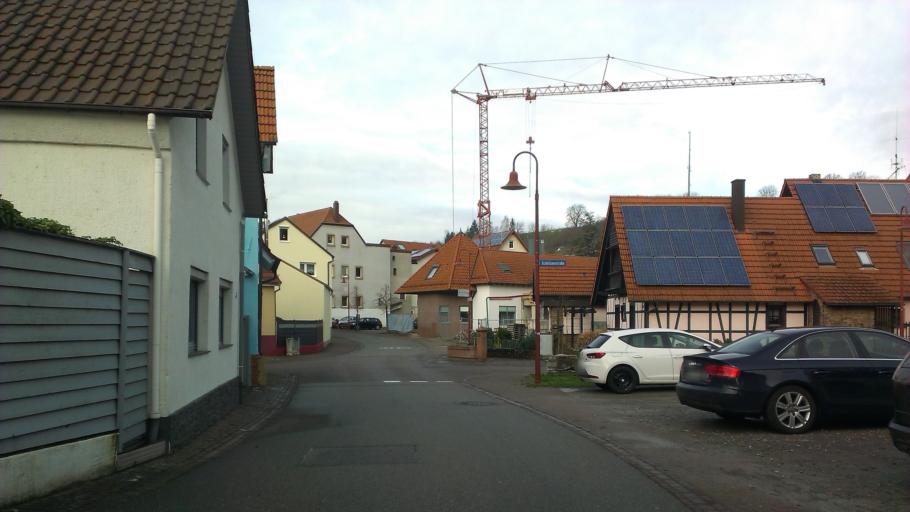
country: DE
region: Baden-Wuerttemberg
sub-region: Karlsruhe Region
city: Horrenberg
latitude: 49.2635
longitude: 8.7586
